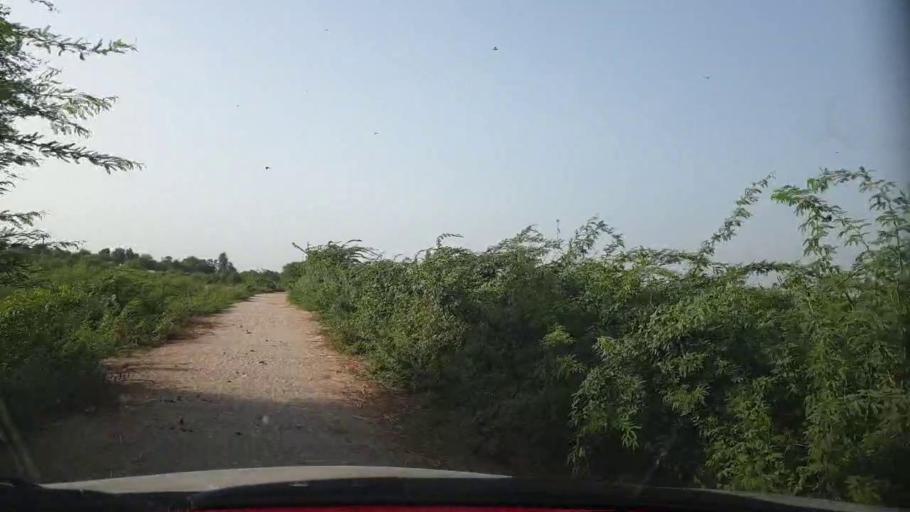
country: PK
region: Sindh
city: Talhar
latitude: 24.8963
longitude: 68.8203
